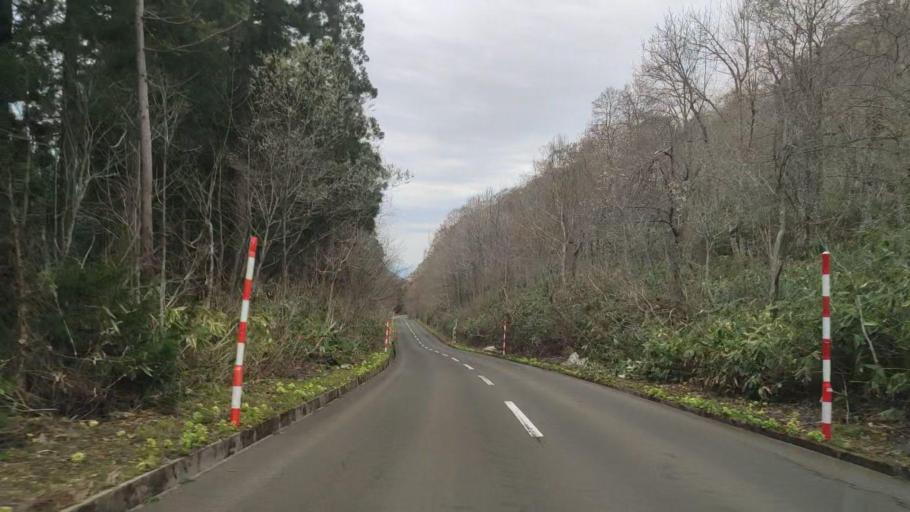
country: JP
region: Akita
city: Hanawa
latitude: 40.4131
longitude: 140.8183
